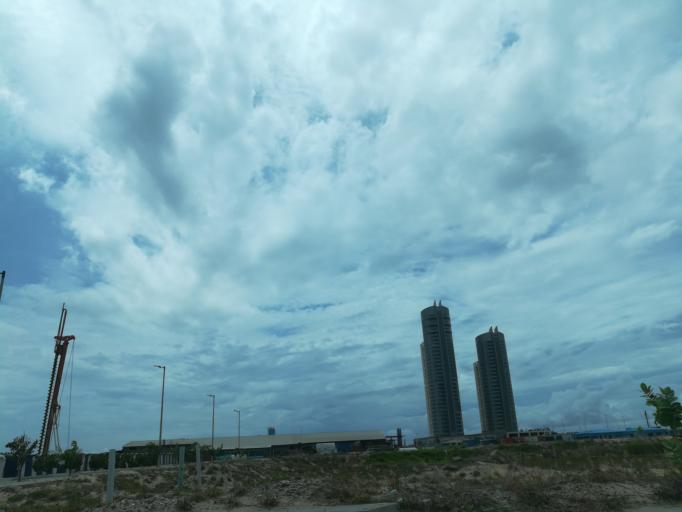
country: NG
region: Lagos
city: Lagos
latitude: 6.4122
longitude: 3.4068
